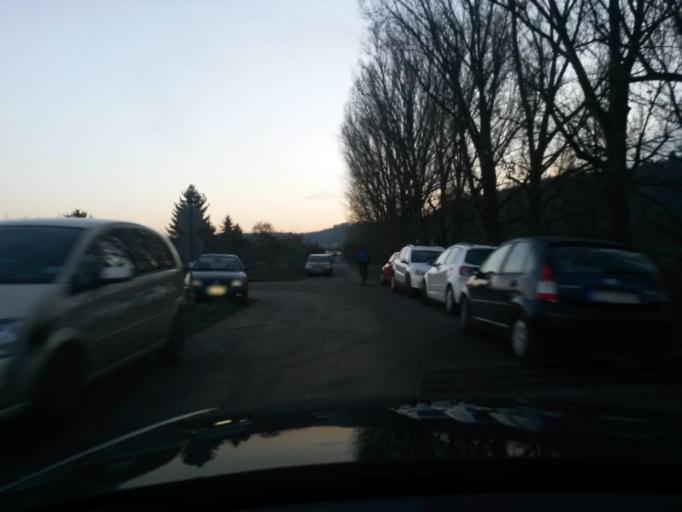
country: DE
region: Bavaria
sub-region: Regierungsbezirk Unterfranken
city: Sommerhausen
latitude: 49.6970
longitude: 10.0226
